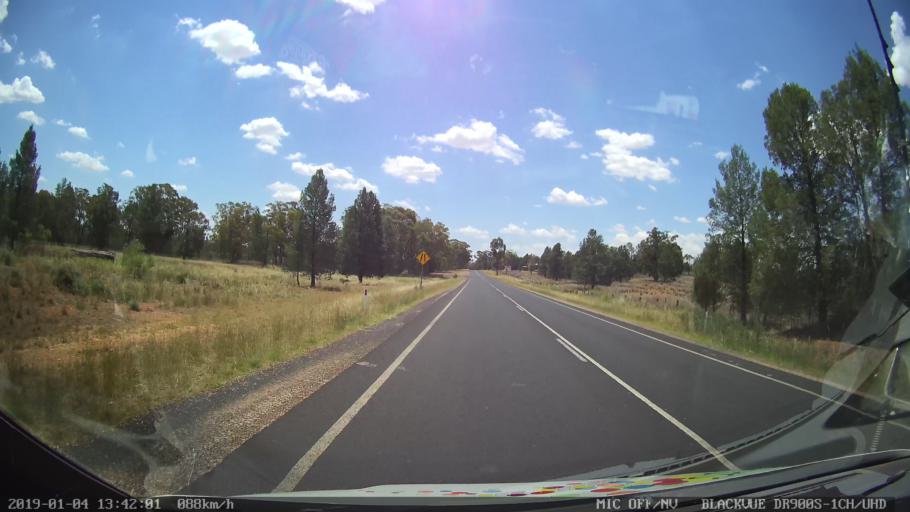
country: AU
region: New South Wales
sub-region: Dubbo Municipality
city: Dubbo
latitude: -32.4949
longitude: 148.5538
